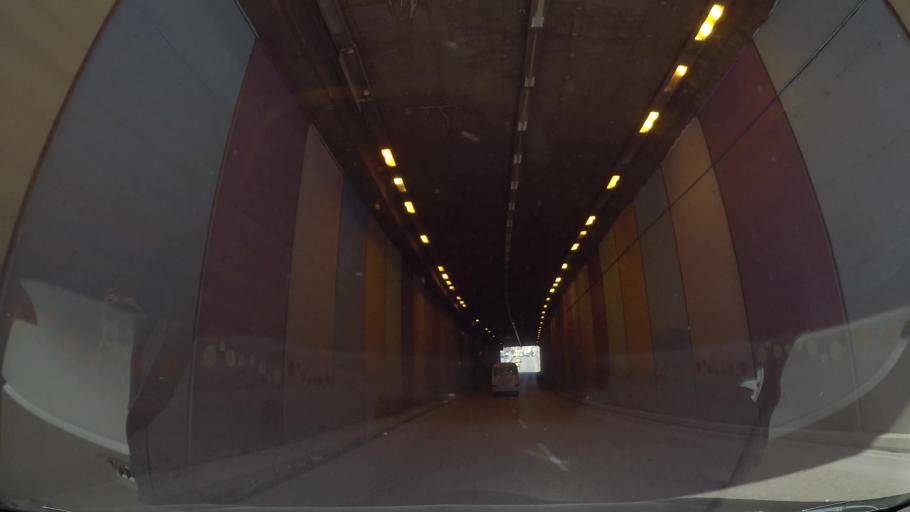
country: JO
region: Zarqa
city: Zarqa
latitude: 32.0722
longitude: 36.0984
